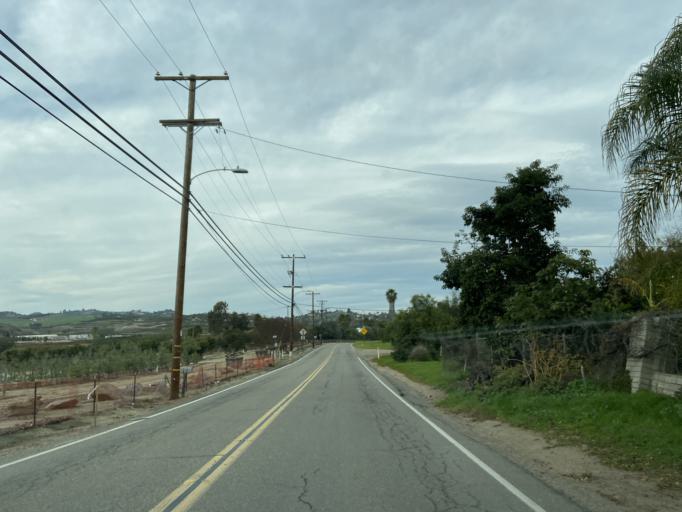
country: US
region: California
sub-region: San Diego County
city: Bonsall
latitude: 33.2641
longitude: -117.2450
